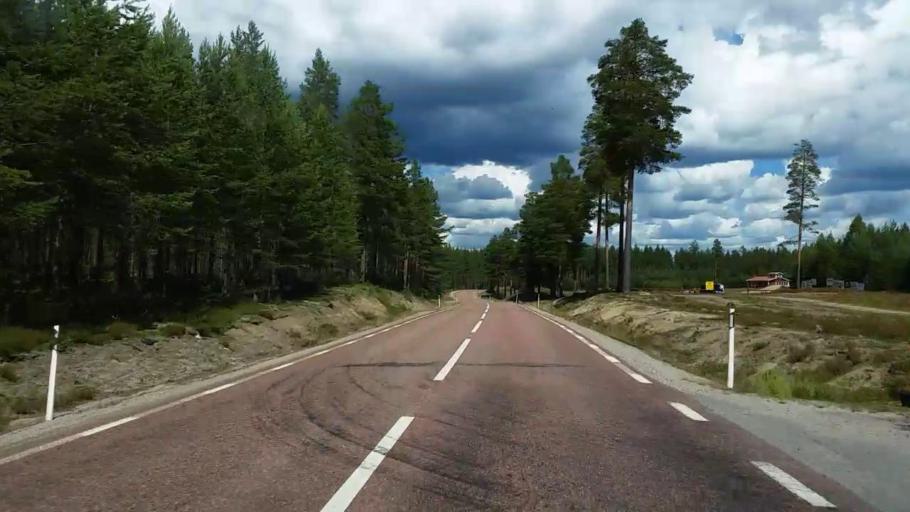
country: SE
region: Gaevleborg
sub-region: Ovanakers Kommun
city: Edsbyn
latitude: 61.3470
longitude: 15.5715
